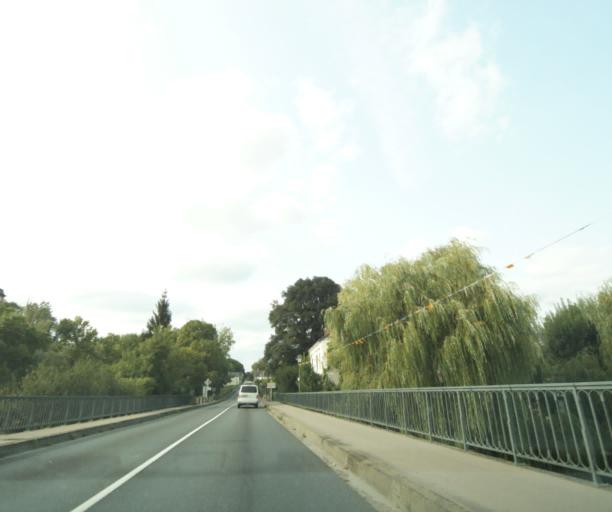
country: FR
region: Centre
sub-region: Departement d'Indre-et-Loire
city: Cormery
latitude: 47.2697
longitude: 0.8348
